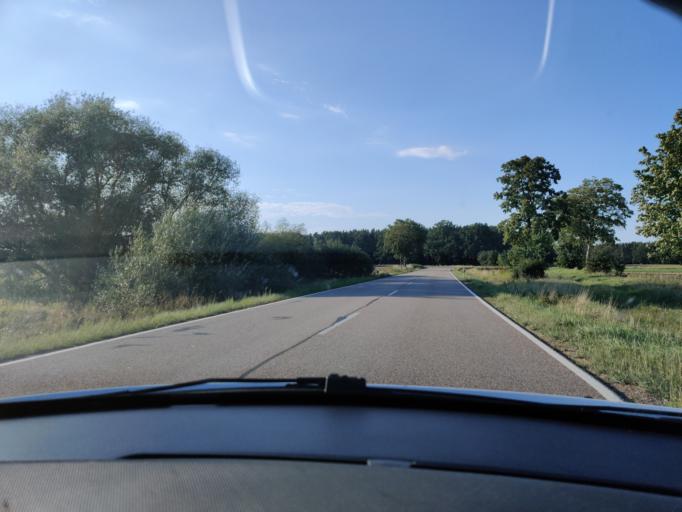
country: DE
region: Bavaria
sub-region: Upper Palatinate
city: Stulln
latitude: 49.4033
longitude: 12.1304
